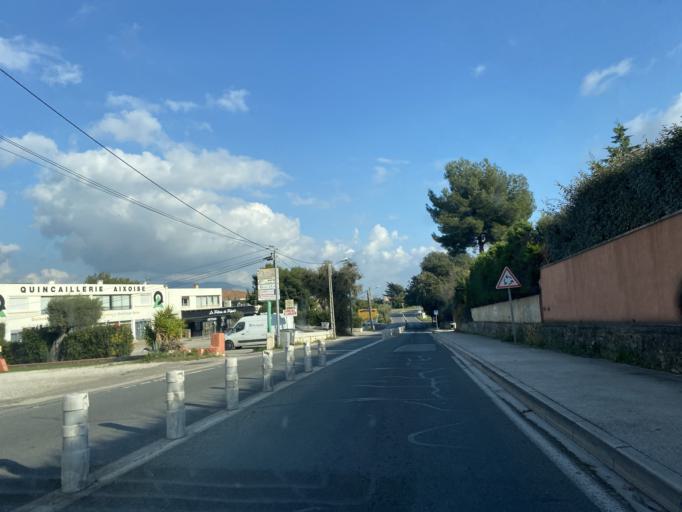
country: FR
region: Provence-Alpes-Cote d'Azur
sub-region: Departement du Var
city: Six-Fours-les-Plages
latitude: 43.1081
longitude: 5.8402
